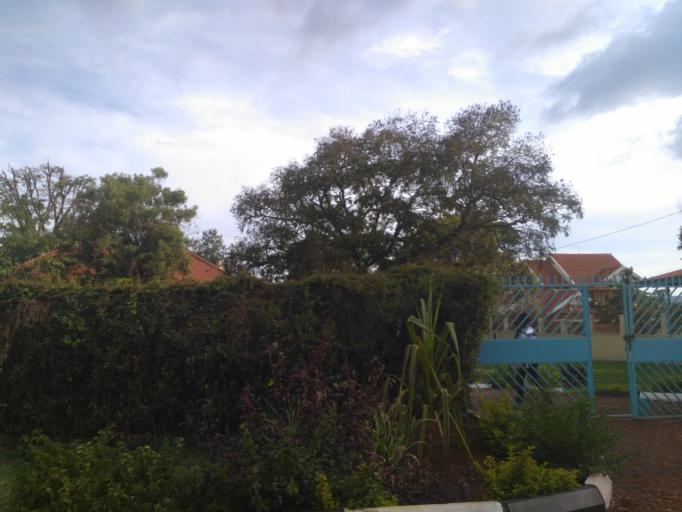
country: UG
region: Eastern Region
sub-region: Jinja District
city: Jinja
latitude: 0.4195
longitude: 33.2078
